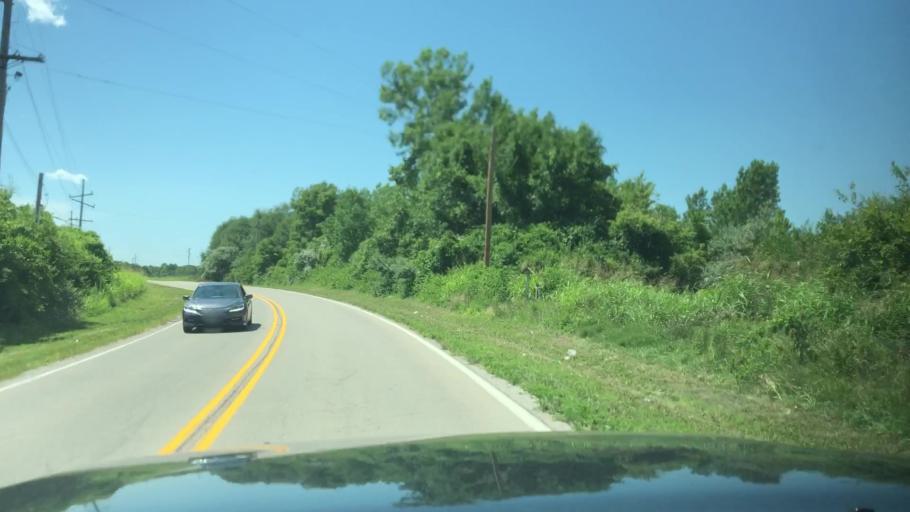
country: US
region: Illinois
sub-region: Saint Clair County
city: Alorton
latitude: 38.5525
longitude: -90.0763
